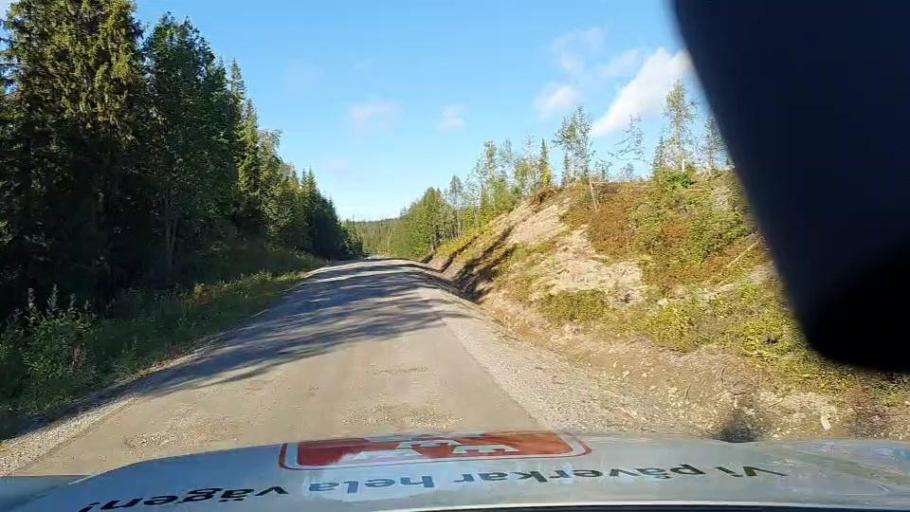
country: SE
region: Jaemtland
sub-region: Stroemsunds Kommun
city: Stroemsund
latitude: 64.5539
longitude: 15.0916
